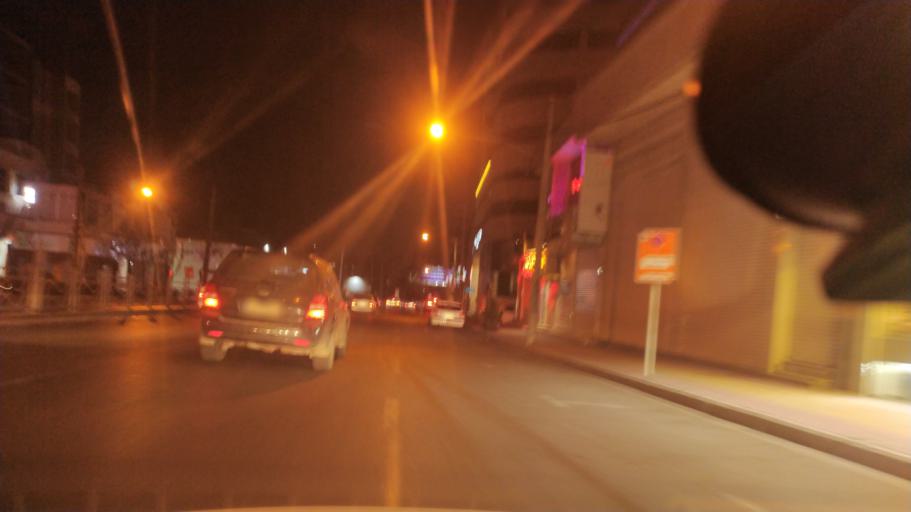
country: IR
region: Alborz
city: Karaj
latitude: 35.8144
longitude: 50.9985
